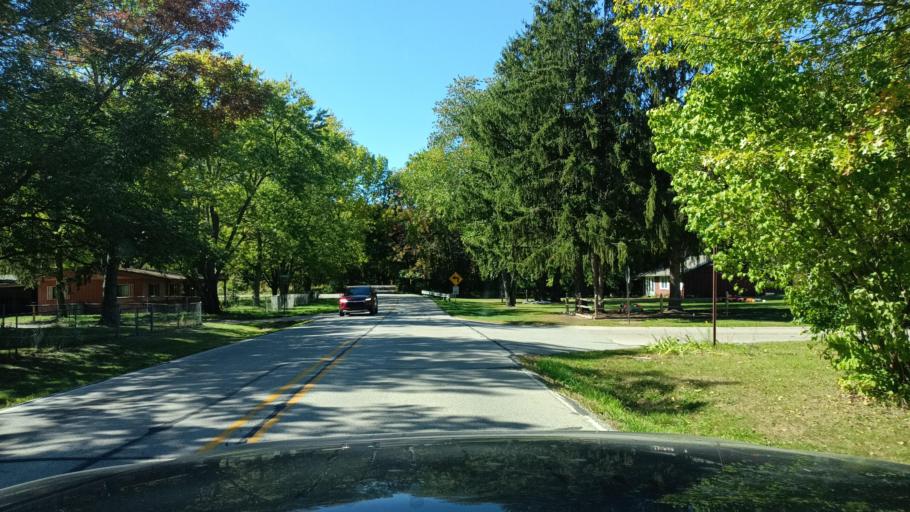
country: US
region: Illinois
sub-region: Champaign County
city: Lake of the Woods
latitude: 40.2113
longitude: -88.3641
